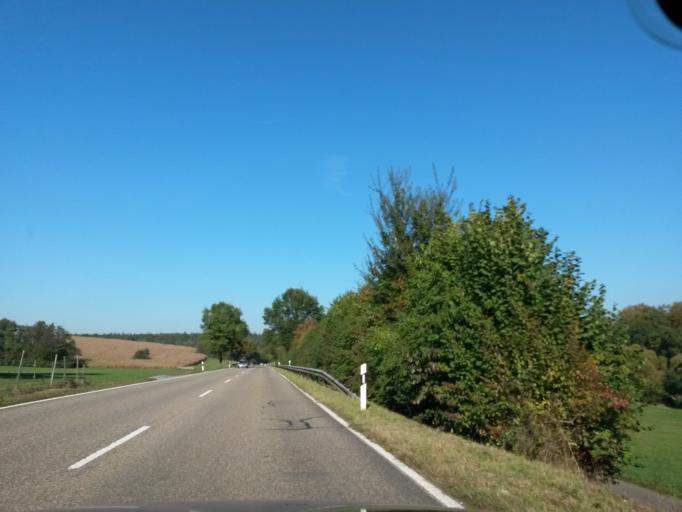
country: DE
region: Baden-Wuerttemberg
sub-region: Karlsruhe Region
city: Ettlingen
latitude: 48.9261
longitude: 8.5072
